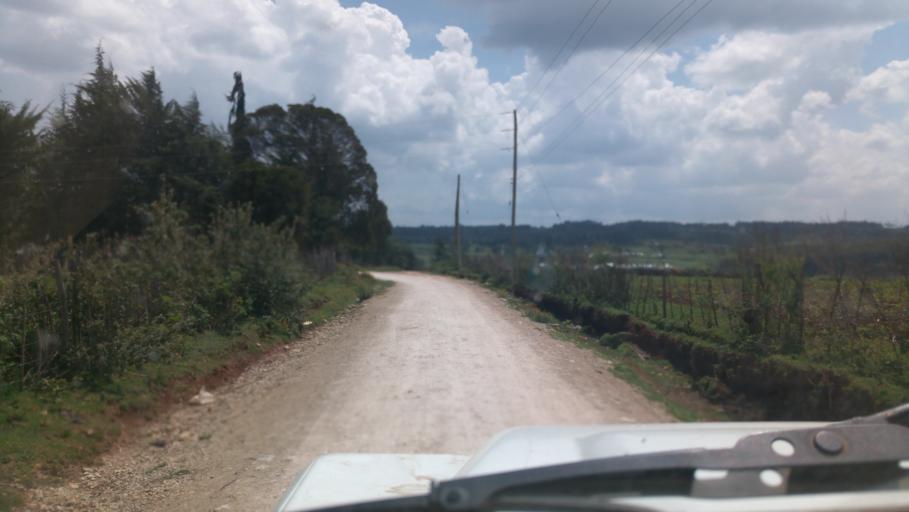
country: KE
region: Nakuru
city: Molo
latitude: -0.4256
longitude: 35.6844
